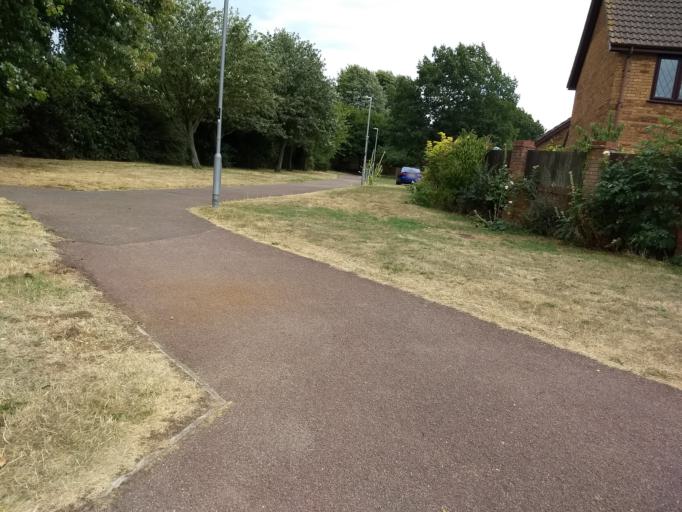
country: GB
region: England
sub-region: Milton Keynes
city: Newport Pagnell
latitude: 52.0764
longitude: -0.7271
